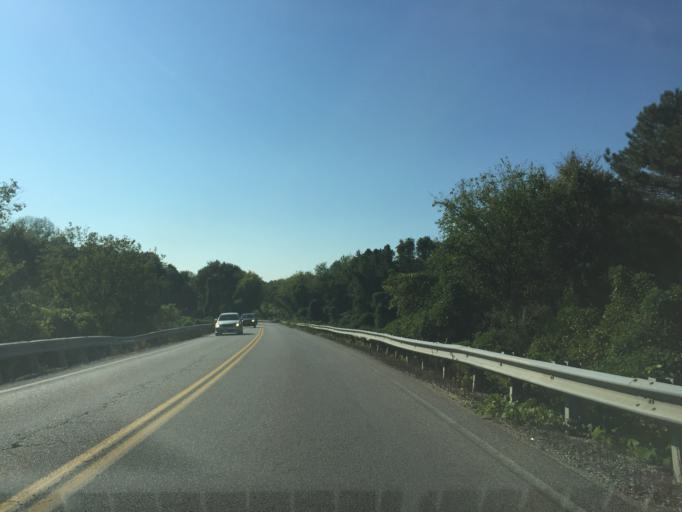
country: US
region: Tennessee
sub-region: Hamilton County
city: Harrison
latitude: 35.0870
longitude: -85.1618
